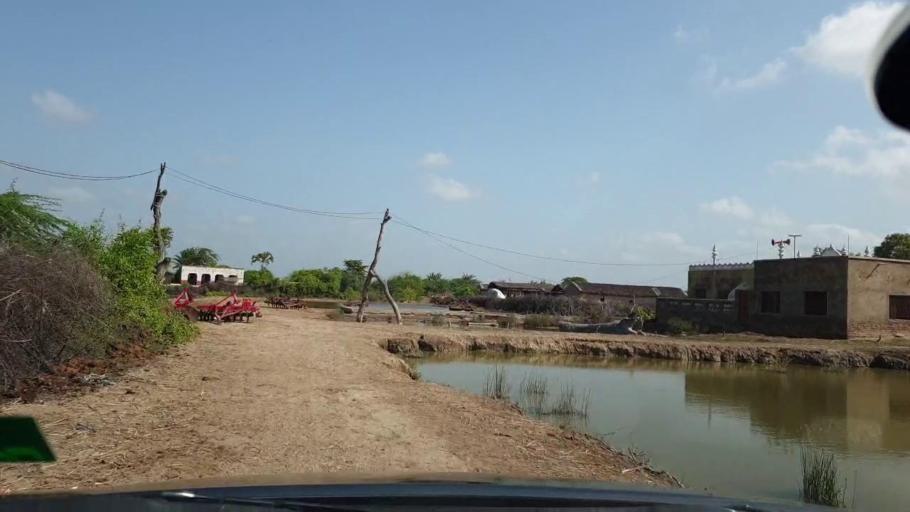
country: PK
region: Sindh
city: Tando Bago
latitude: 24.6475
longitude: 69.0940
